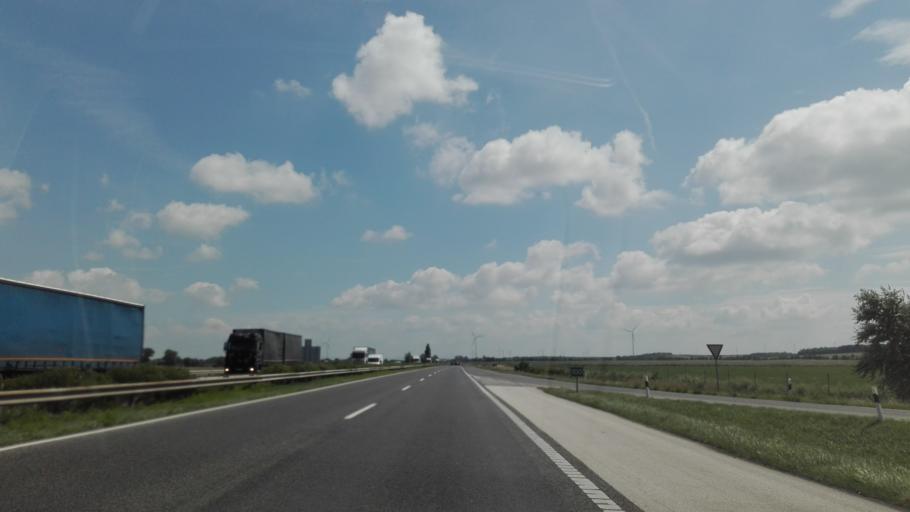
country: HU
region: Gyor-Moson-Sopron
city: Bony
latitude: 47.6829
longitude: 17.8925
